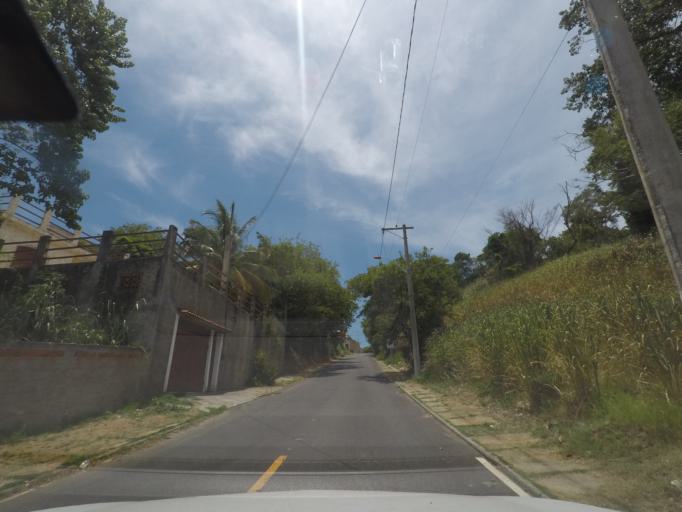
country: BR
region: Rio de Janeiro
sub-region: Marica
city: Marica
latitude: -22.9325
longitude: -42.8278
